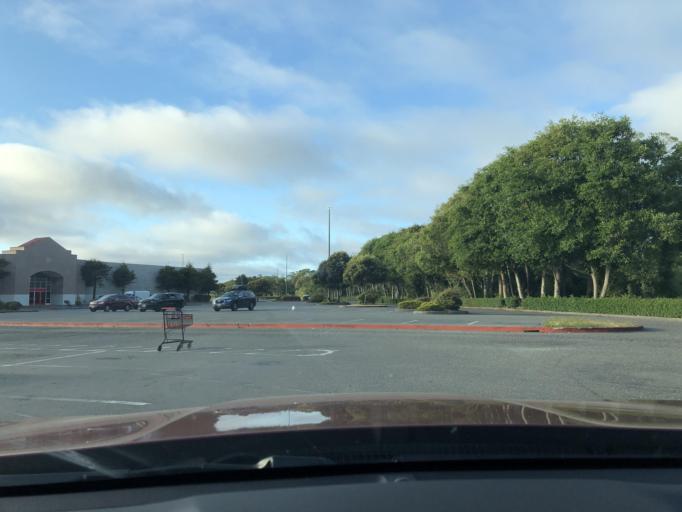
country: US
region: California
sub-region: Humboldt County
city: Bayview
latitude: 40.7803
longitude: -124.1881
